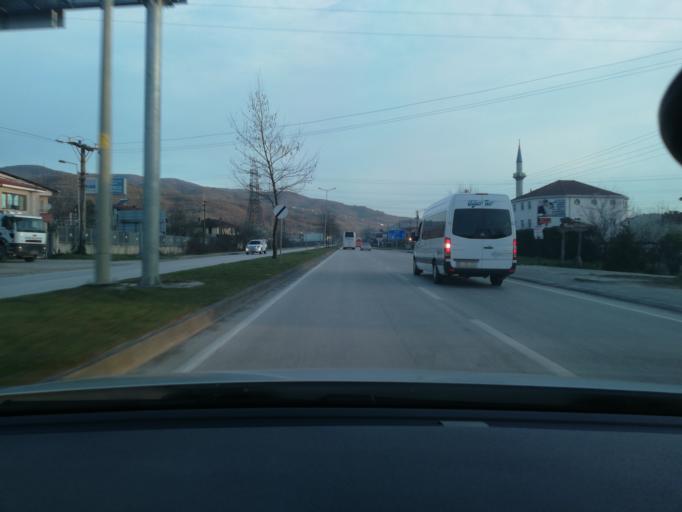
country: TR
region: Duzce
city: Konuralp
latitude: 40.9156
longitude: 31.1429
